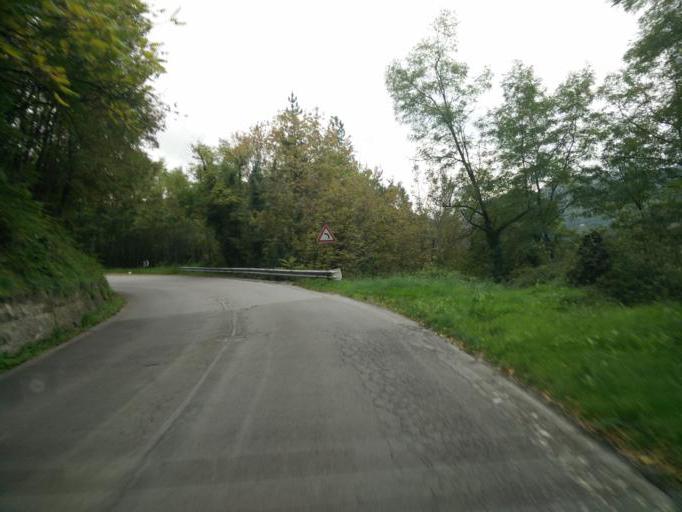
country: IT
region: Tuscany
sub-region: Provincia di Lucca
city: Camporgiano
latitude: 44.1724
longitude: 10.3261
